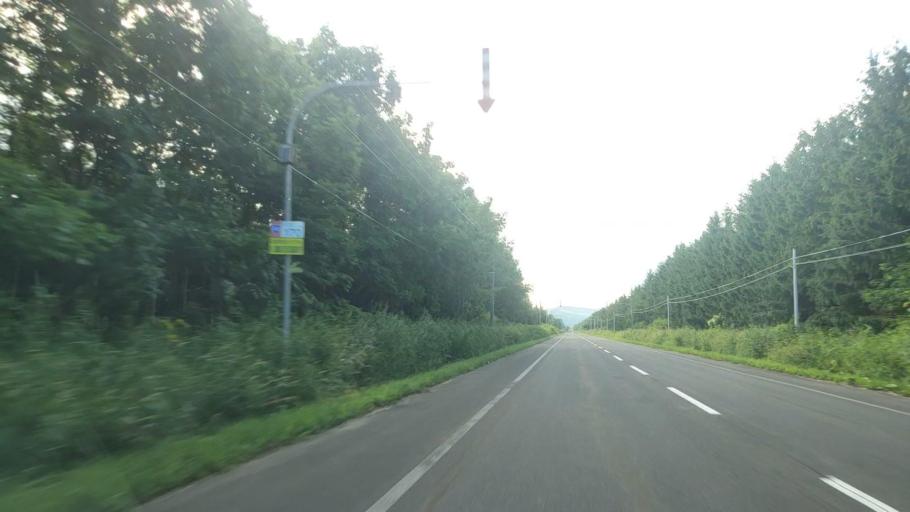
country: JP
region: Hokkaido
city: Makubetsu
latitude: 44.8833
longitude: 142.0156
